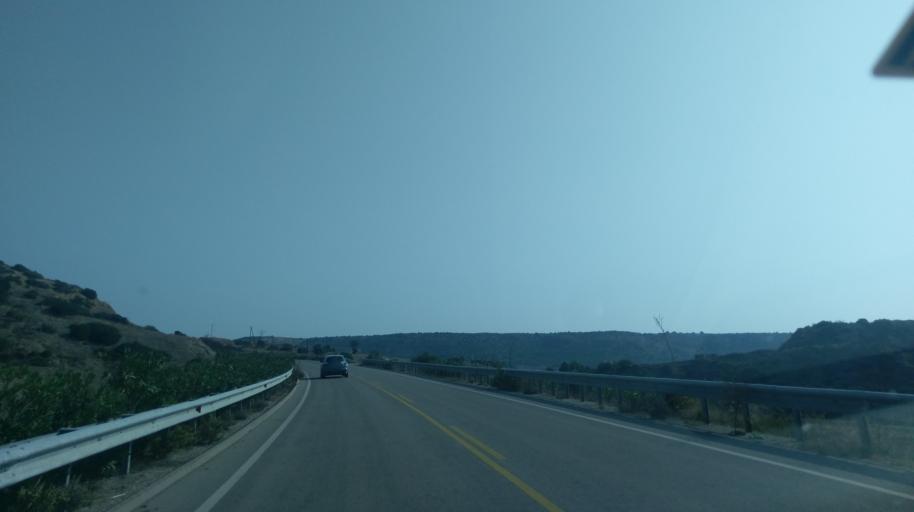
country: CY
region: Ammochostos
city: Leonarisso
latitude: 35.4778
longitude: 34.1162
